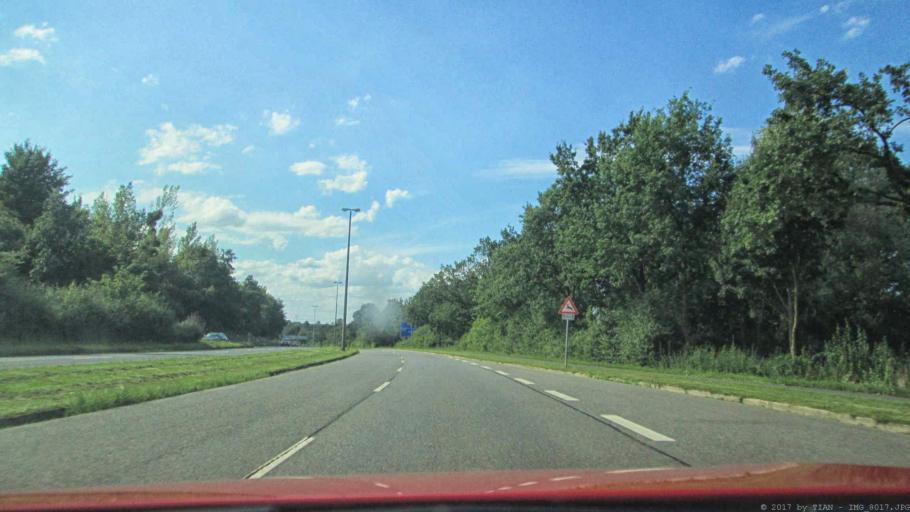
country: DE
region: Lower Saxony
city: Wolfsburg
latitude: 52.4102
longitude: 10.7425
